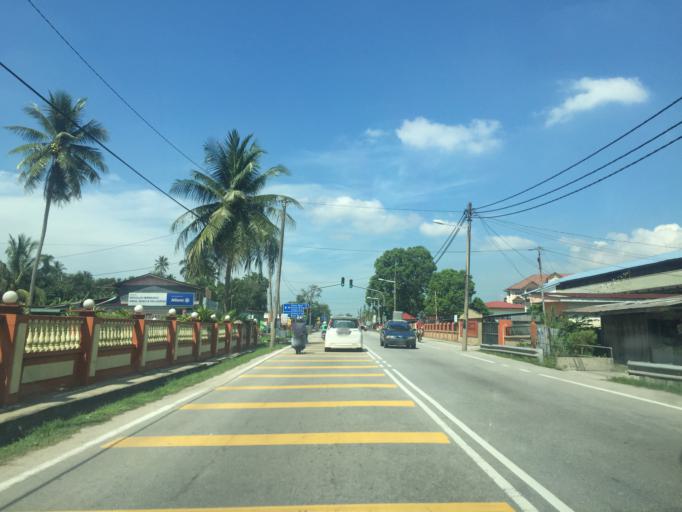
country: MY
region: Penang
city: Tasek Glugor
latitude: 5.4825
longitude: 100.4930
